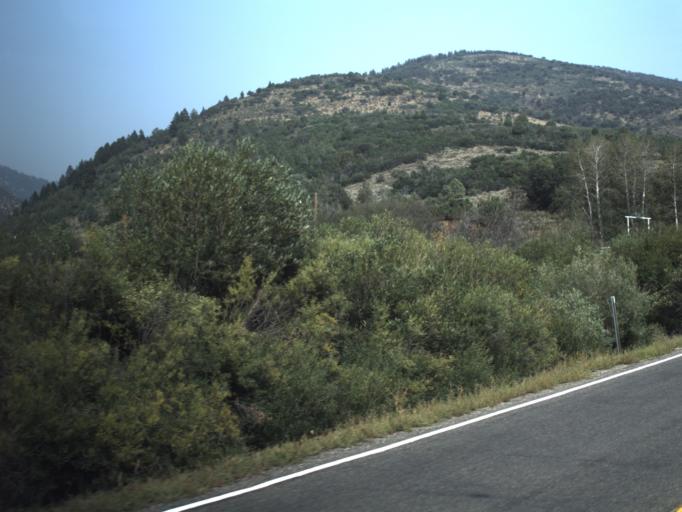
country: US
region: Utah
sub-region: Summit County
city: Francis
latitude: 40.6255
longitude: -111.2324
